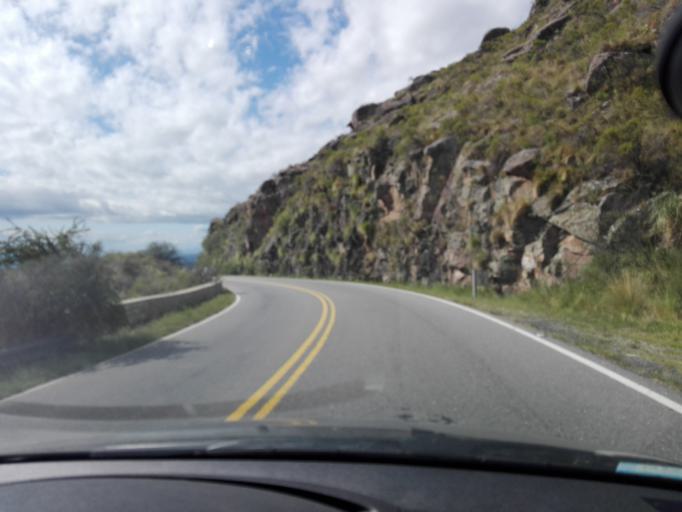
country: AR
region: Cordoba
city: Mina Clavero
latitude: -31.7709
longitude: -64.9185
